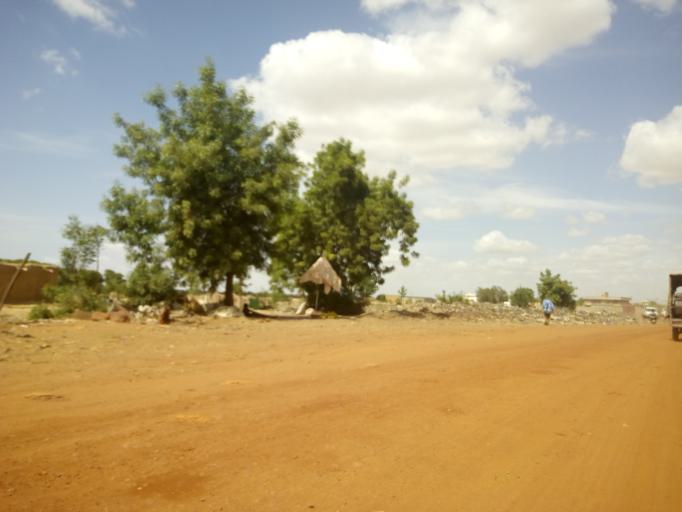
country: ML
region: Segou
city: Segou
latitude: 13.4417
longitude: -6.2412
